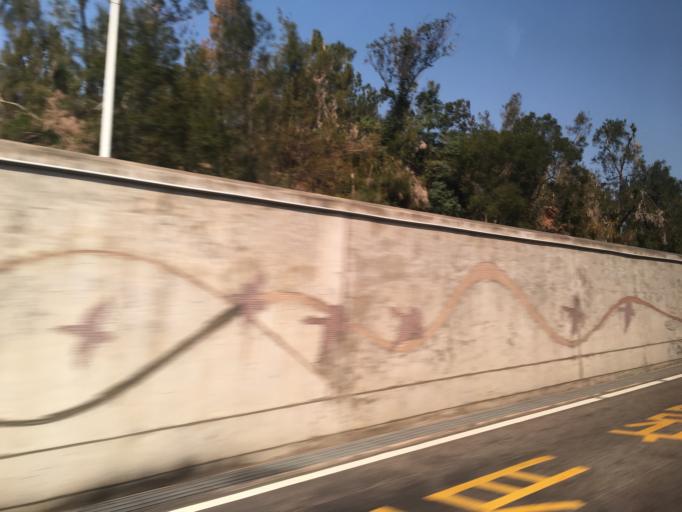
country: TW
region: Fukien
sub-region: Kinmen
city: Jincheng
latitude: 24.4390
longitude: 118.3656
